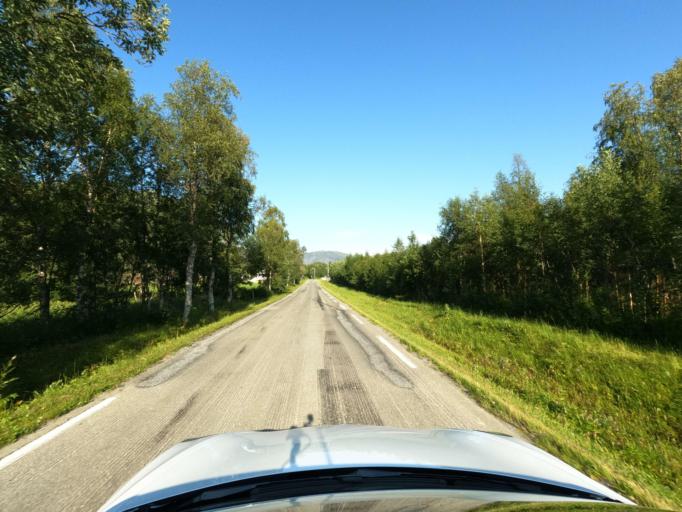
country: NO
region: Nordland
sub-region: Narvik
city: Bjerkvik
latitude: 68.5581
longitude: 17.6409
